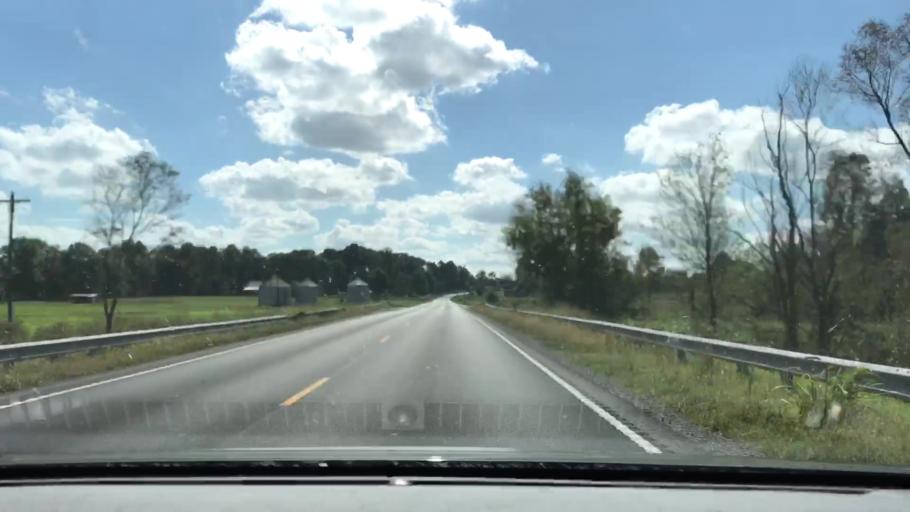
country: US
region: Kentucky
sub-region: Graves County
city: Mayfield
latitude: 36.8615
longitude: -88.5724
